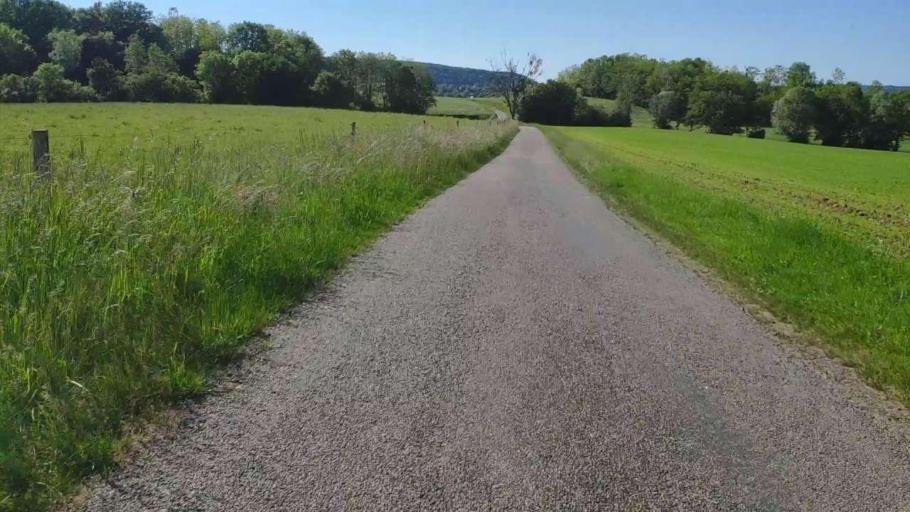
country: FR
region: Franche-Comte
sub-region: Departement du Jura
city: Perrigny
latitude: 46.7251
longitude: 5.5704
